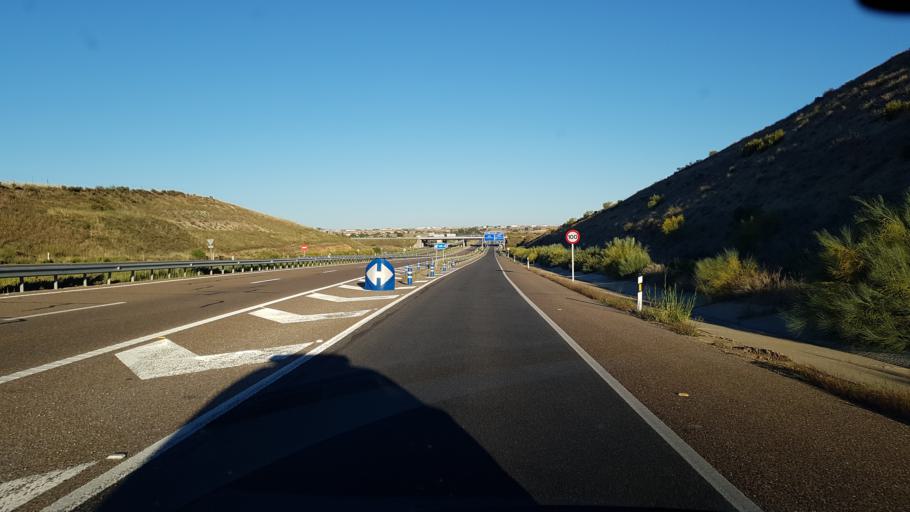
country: ES
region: Castille and Leon
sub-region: Provincia de Zamora
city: Monfarracinos
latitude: 41.5326
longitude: -5.6970
